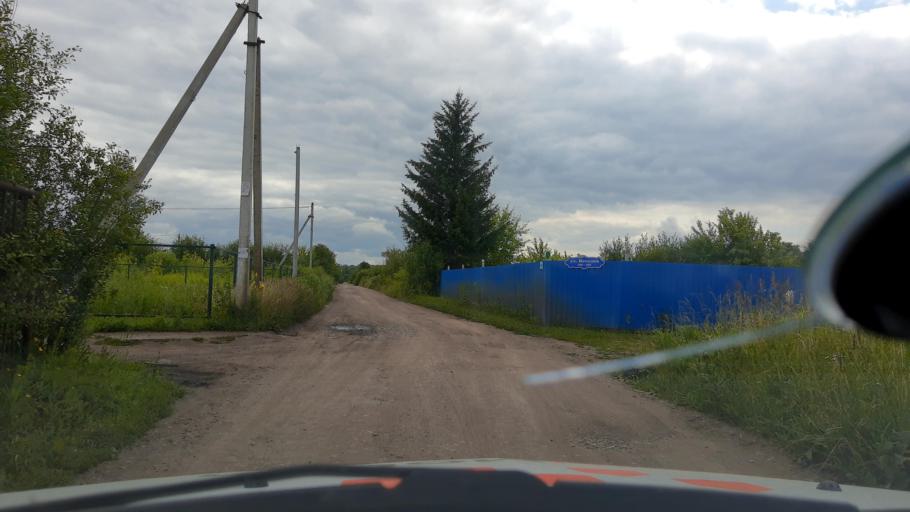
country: RU
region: Bashkortostan
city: Kabakovo
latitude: 54.7245
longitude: 56.2039
